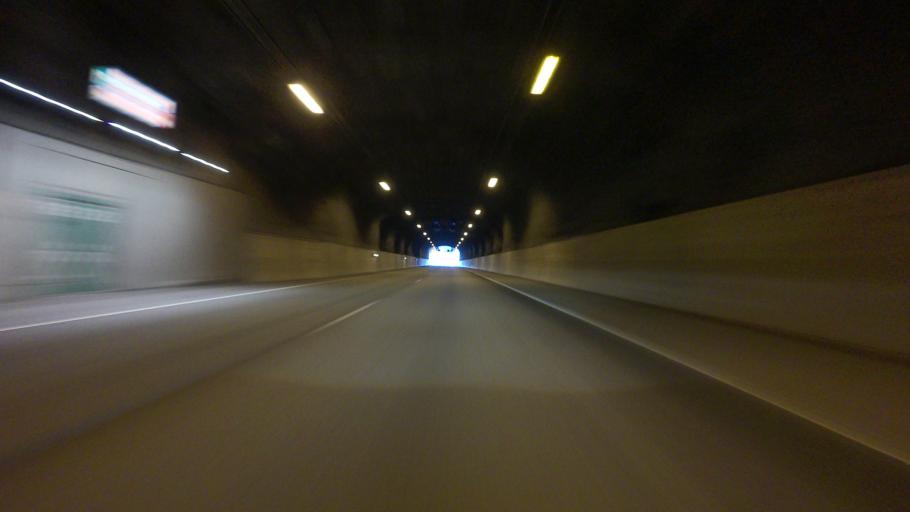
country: FI
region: Uusimaa
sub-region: Helsinki
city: Saukkola
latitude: 60.3124
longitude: 23.9901
